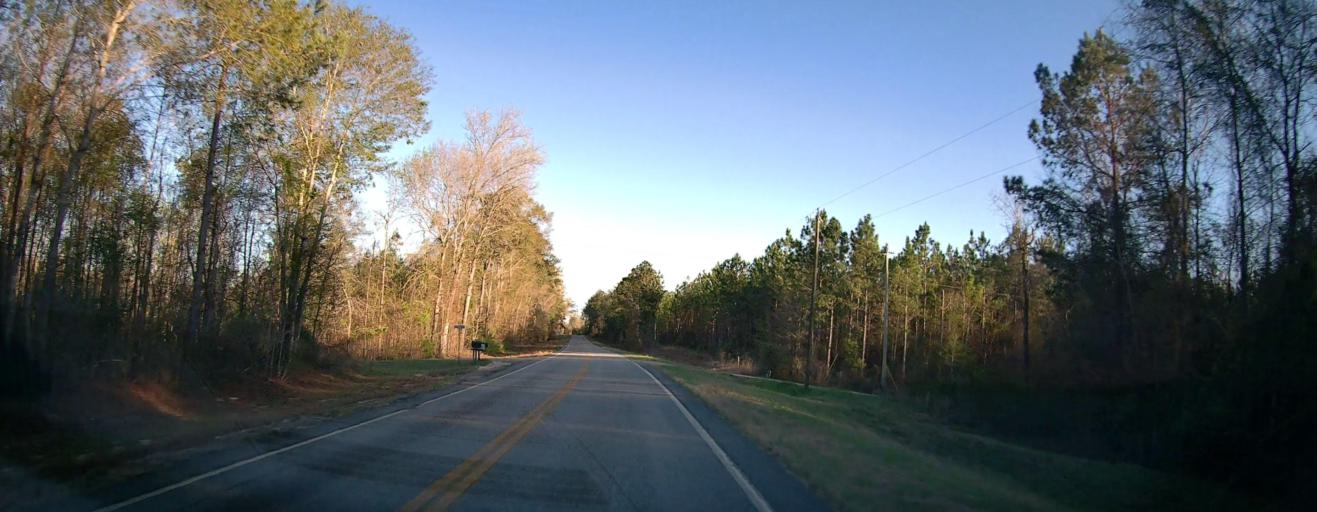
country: US
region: Georgia
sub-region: Wilcox County
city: Abbeville
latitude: 32.0705
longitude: -83.2822
